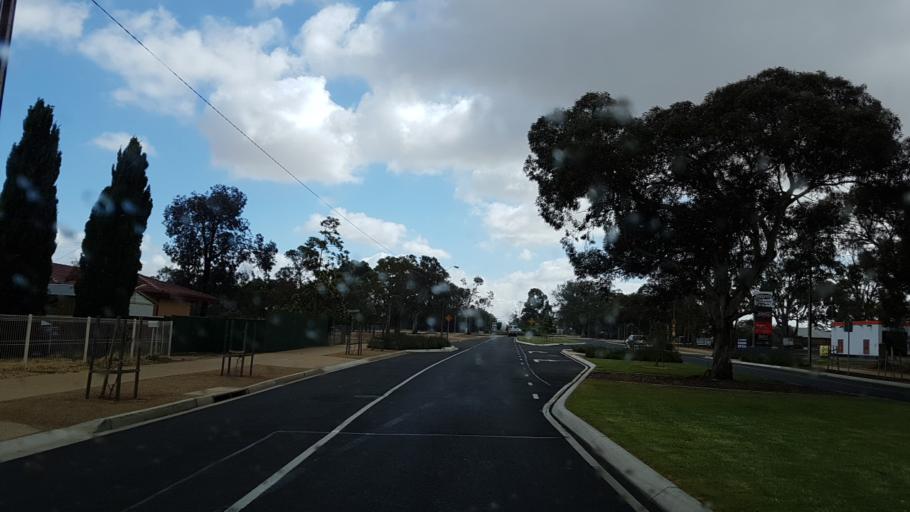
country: AU
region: South Australia
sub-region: Playford
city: Smithfield
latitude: -34.6931
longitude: 138.6673
